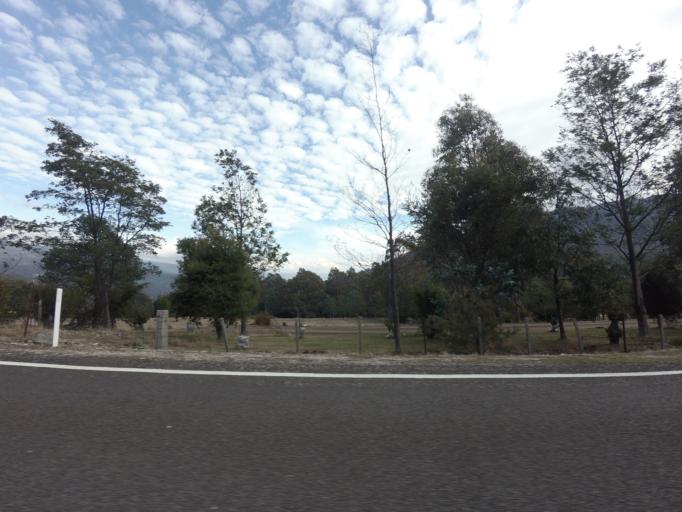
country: AU
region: Tasmania
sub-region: Meander Valley
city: Deloraine
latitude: -41.6605
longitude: 146.7235
